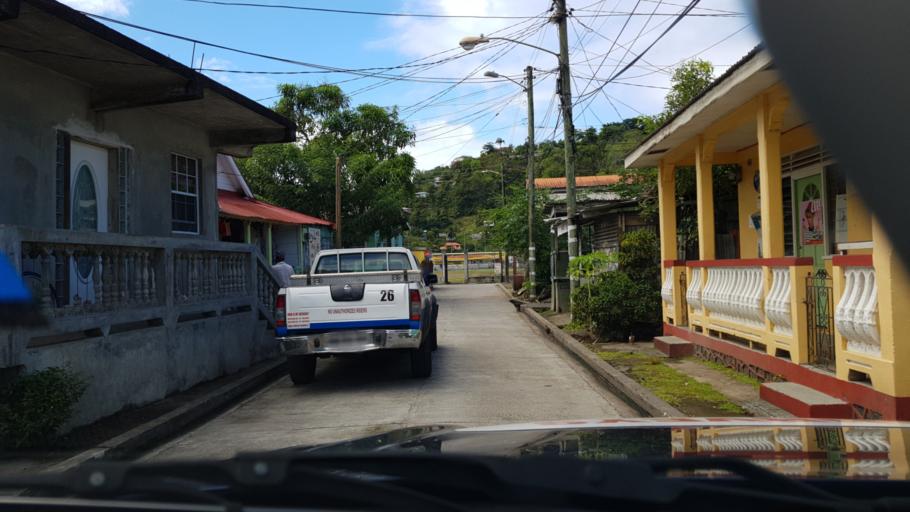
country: LC
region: Anse-la-Raye
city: Anse La Raye
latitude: 13.9394
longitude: -61.0417
